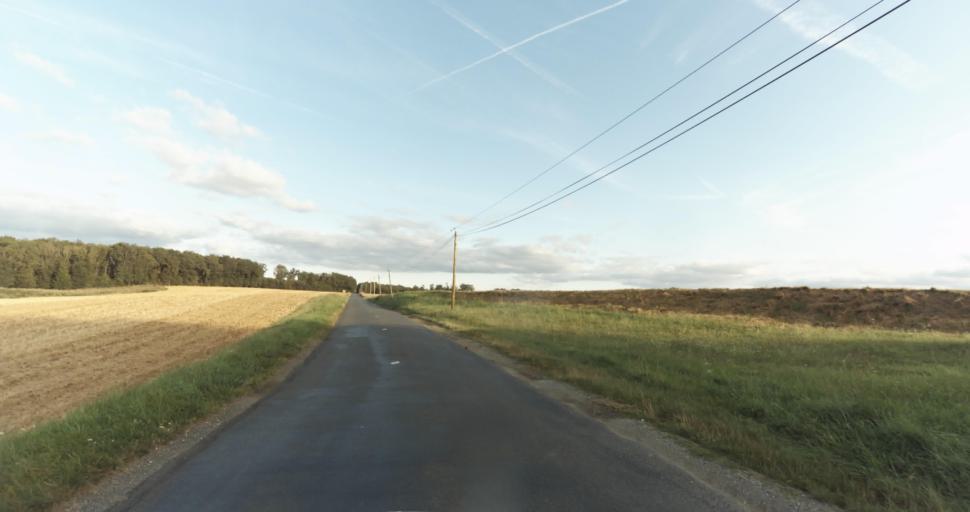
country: FR
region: Haute-Normandie
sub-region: Departement de l'Eure
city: Marcilly-sur-Eure
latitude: 48.8799
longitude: 1.2634
